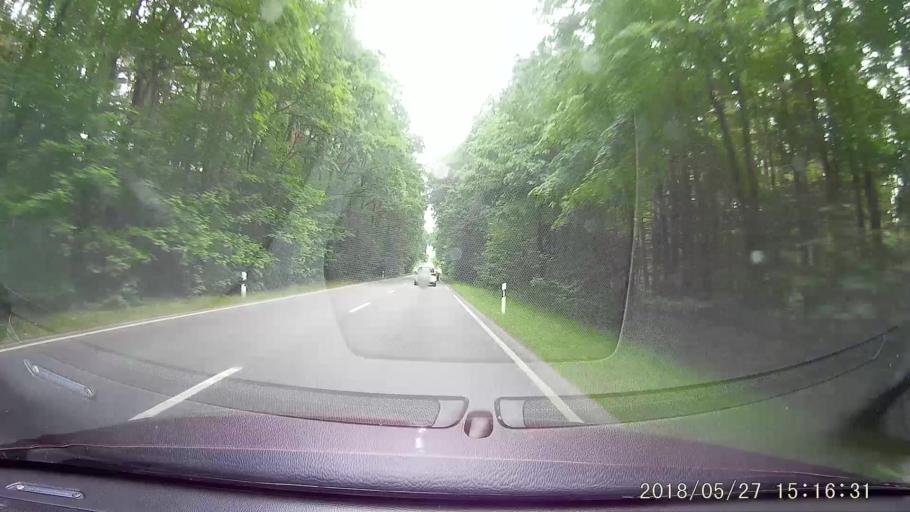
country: DE
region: Saxony
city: Niesky
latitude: 51.2770
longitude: 14.8251
